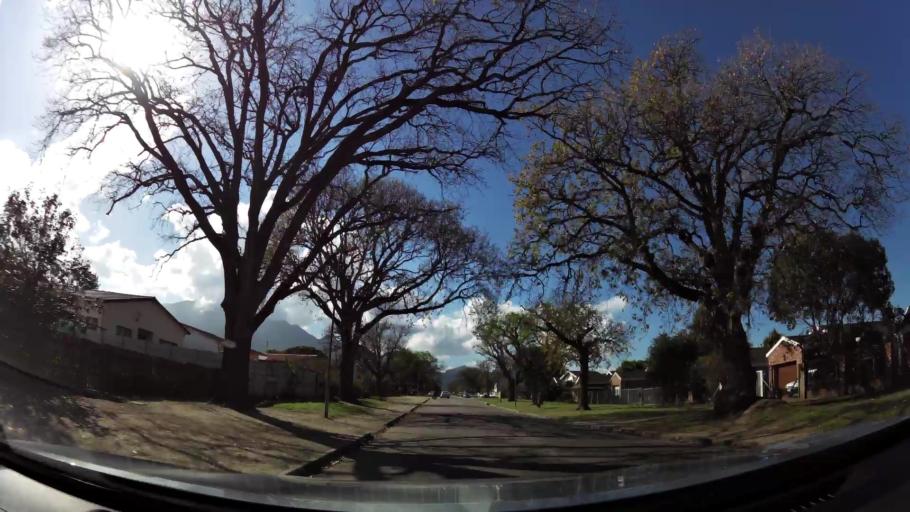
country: ZA
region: Western Cape
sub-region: Eden District Municipality
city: George
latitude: -33.9694
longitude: 22.4528
